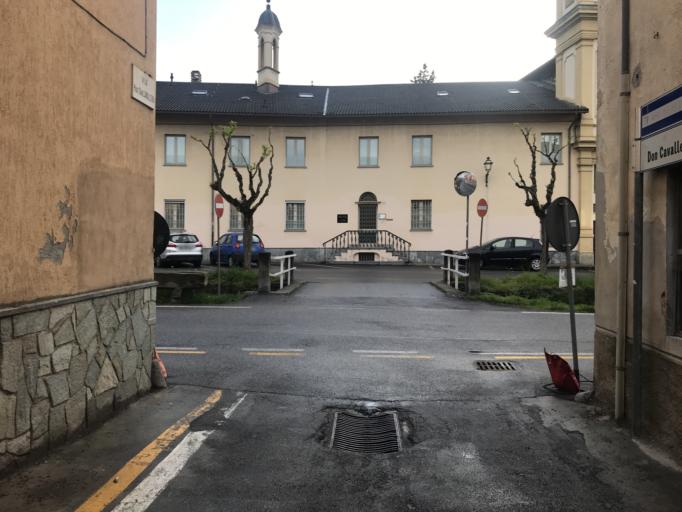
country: IT
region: Piedmont
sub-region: Provincia di Cuneo
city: Boves
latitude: 44.3302
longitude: 7.5471
